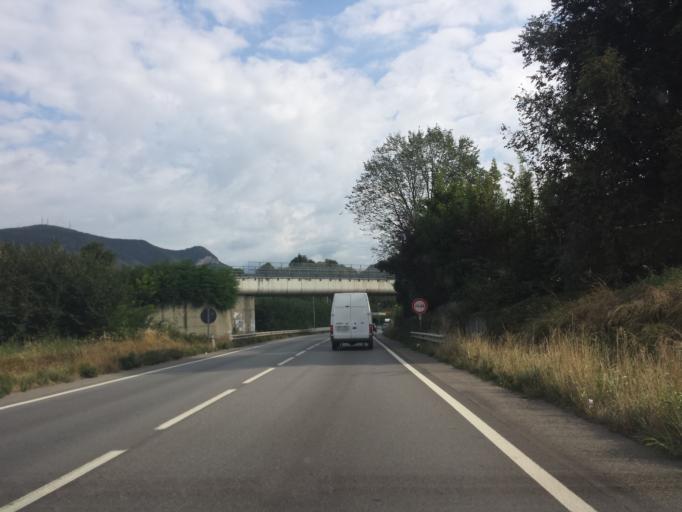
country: IT
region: Lombardy
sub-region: Provincia di Brescia
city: Gavardo-Sopraponte
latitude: 45.5812
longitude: 10.4486
